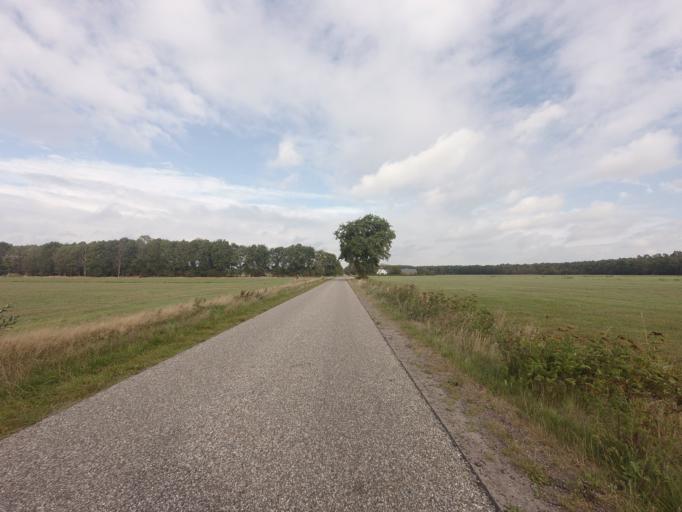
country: NL
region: Friesland
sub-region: Gemeente Heerenveen
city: Jubbega
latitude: 52.9806
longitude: 6.1198
